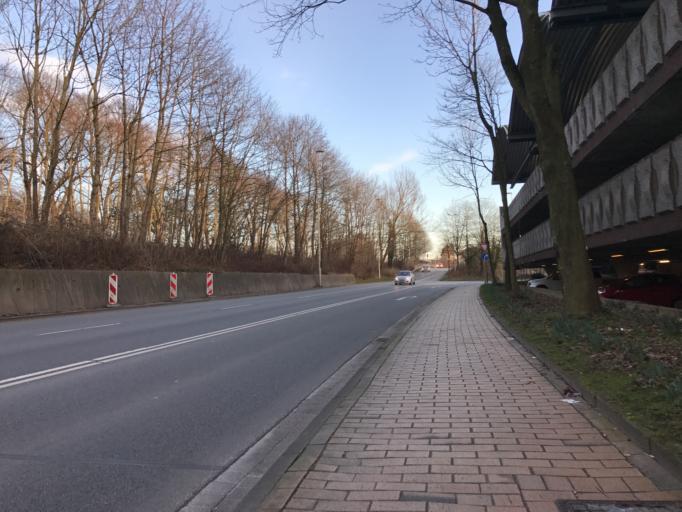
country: DE
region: Schleswig-Holstein
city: Rendsburg
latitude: 54.3050
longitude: 9.6670
